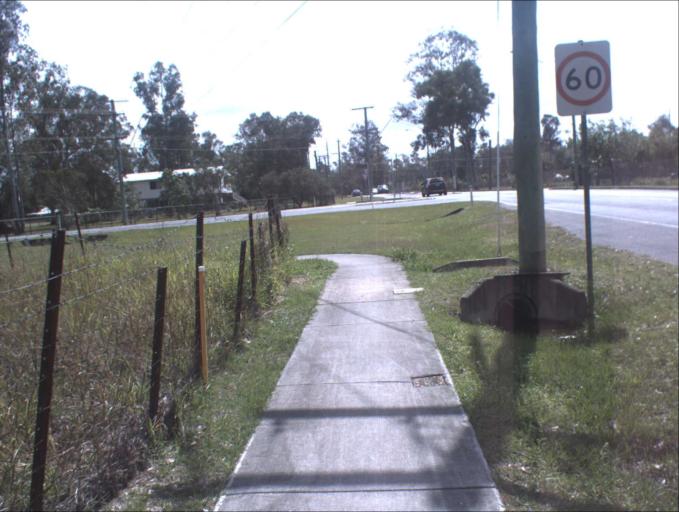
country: AU
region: Queensland
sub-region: Logan
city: Logan City
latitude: -27.6652
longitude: 153.0915
